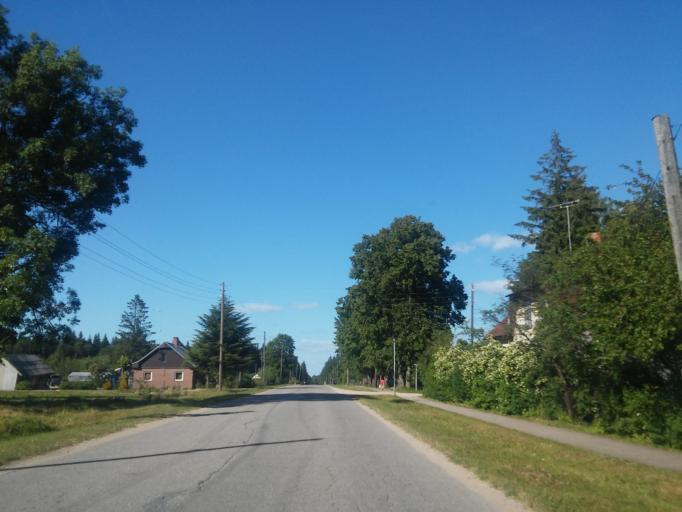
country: LV
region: Vainode
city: Vainode
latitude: 56.4229
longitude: 21.8616
